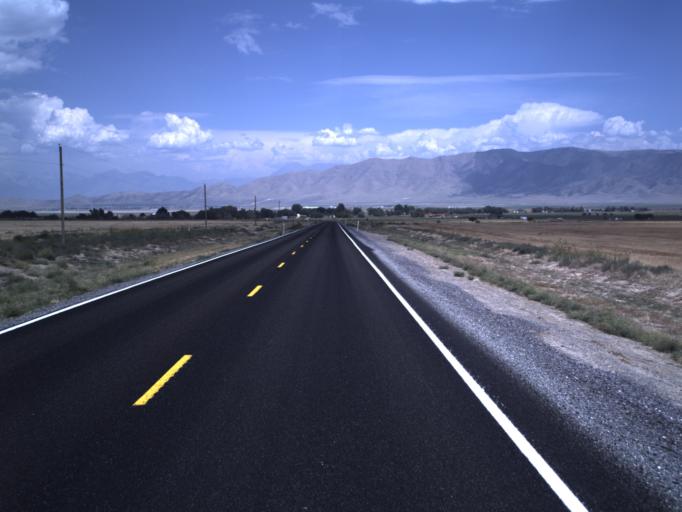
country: US
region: Utah
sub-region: Utah County
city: Eagle Mountain
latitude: 40.2536
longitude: -112.1114
